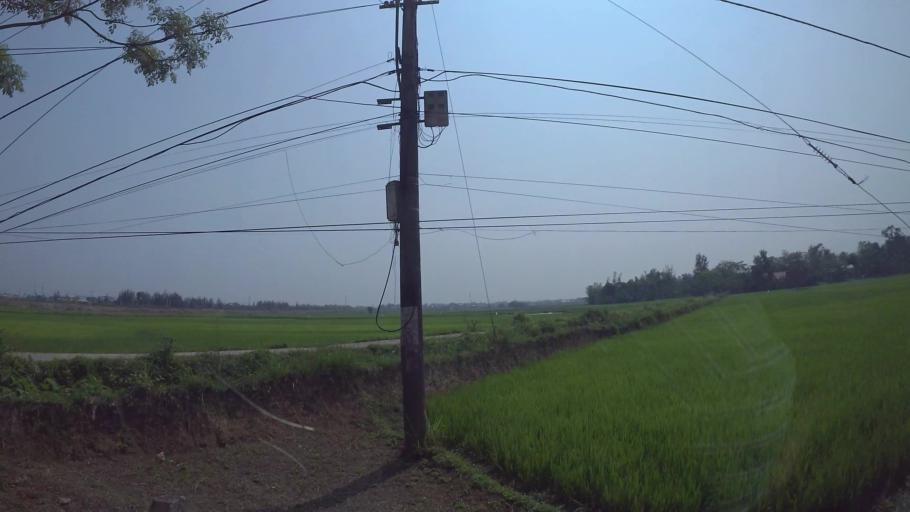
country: VN
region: Da Nang
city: Cam Le
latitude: 15.9796
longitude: 108.2248
